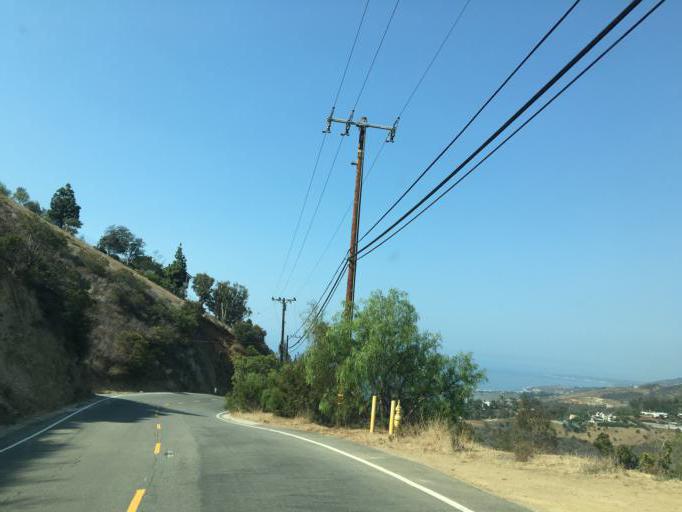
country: US
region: California
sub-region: Los Angeles County
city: Las Flores
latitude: 34.0481
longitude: -118.6469
